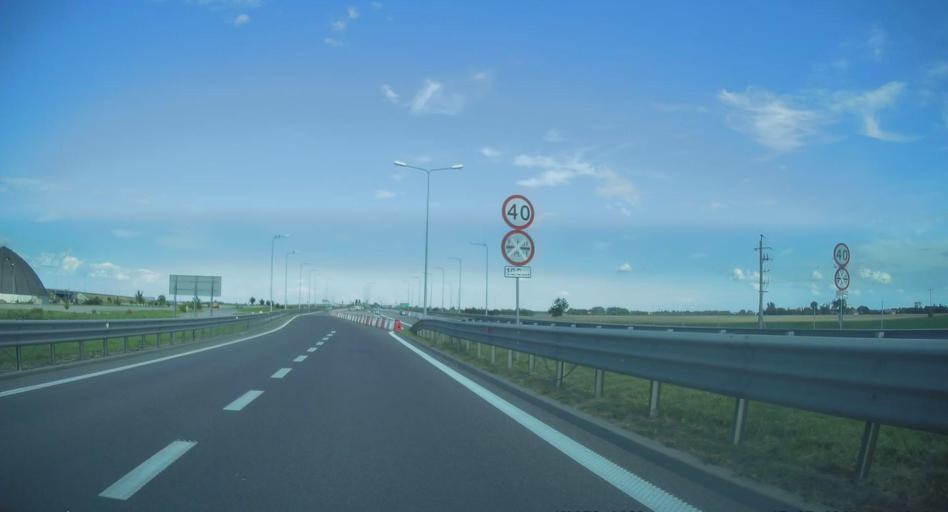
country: PL
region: Subcarpathian Voivodeship
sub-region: Powiat przemyski
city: Orly
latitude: 49.9085
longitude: 22.8118
